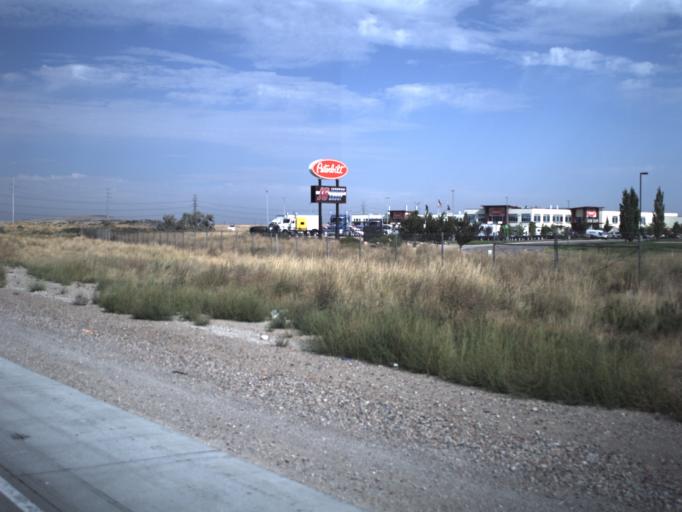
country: US
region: Utah
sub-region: Salt Lake County
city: West Valley City
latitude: 40.7261
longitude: -112.0210
